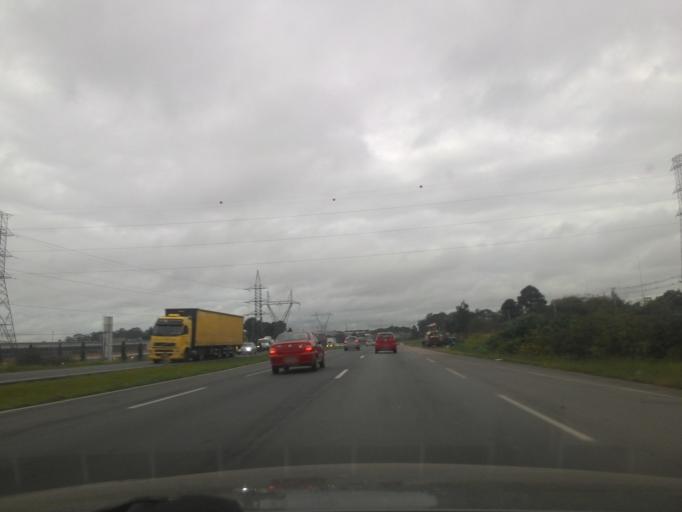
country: BR
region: Parana
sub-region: Araucaria
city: Araucaria
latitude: -25.5485
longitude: -49.3229
